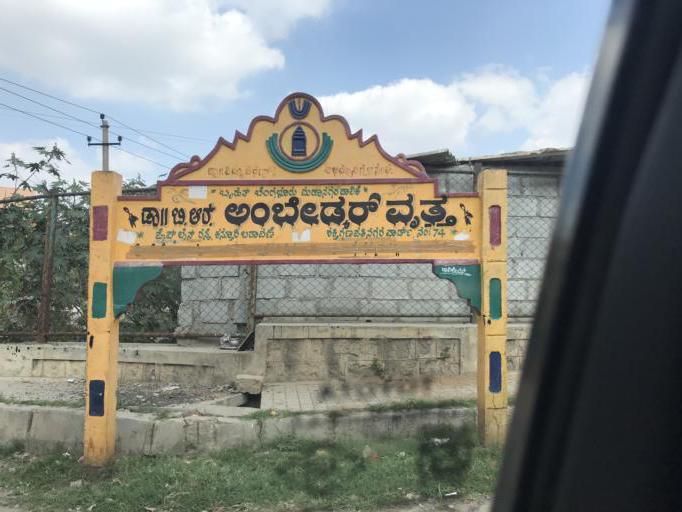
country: IN
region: Karnataka
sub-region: Bangalore Urban
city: Bangalore
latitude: 12.9989
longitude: 77.5273
